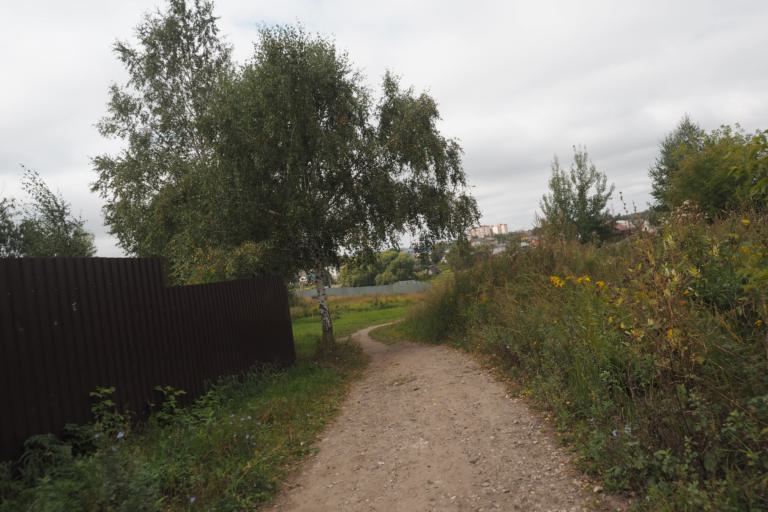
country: RU
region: Moskovskaya
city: Malyshevo
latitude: 55.5386
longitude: 38.3241
